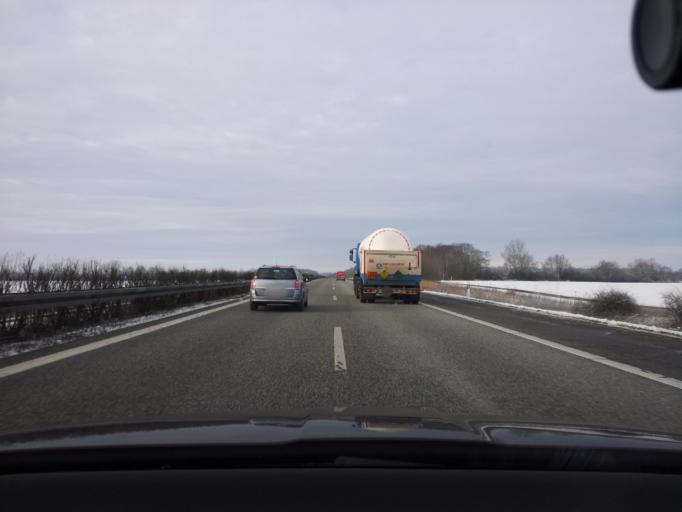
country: DE
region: Mecklenburg-Vorpommern
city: Hagenow
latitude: 53.4910
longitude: 11.1643
